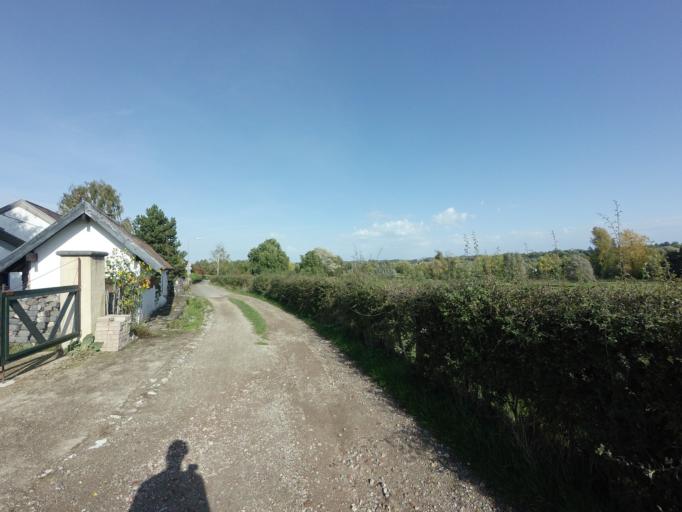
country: BE
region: Wallonia
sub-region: Province de Liege
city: Plombieres
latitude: 50.7839
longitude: 5.9162
